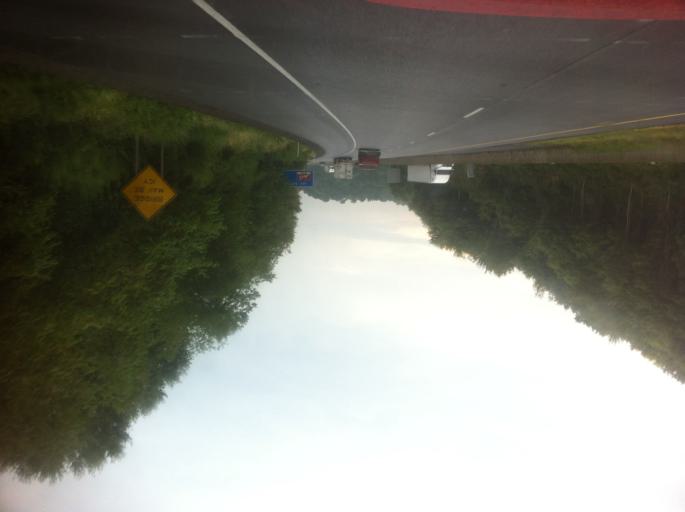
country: US
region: Pennsylvania
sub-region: Clarion County
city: Clarion
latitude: 41.1867
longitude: -79.4096
